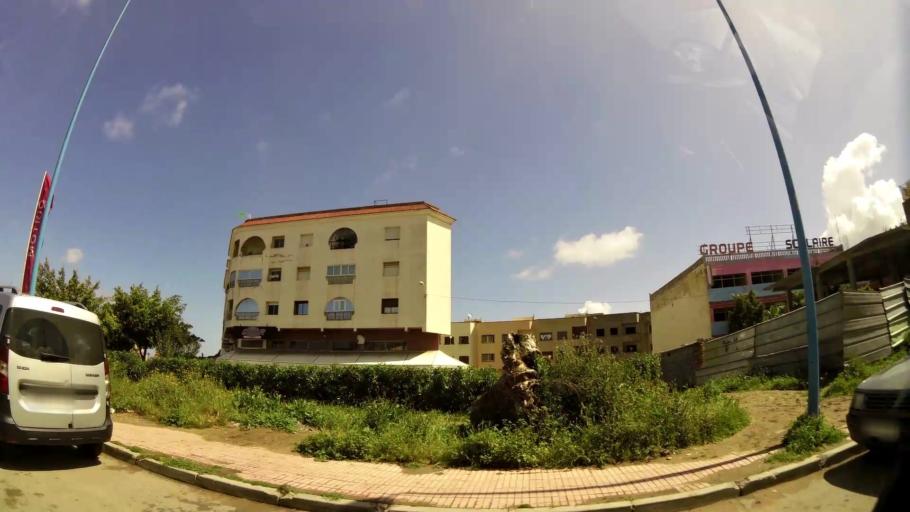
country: MA
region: Grand Casablanca
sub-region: Mohammedia
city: Mohammedia
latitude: 33.6382
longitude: -7.4486
